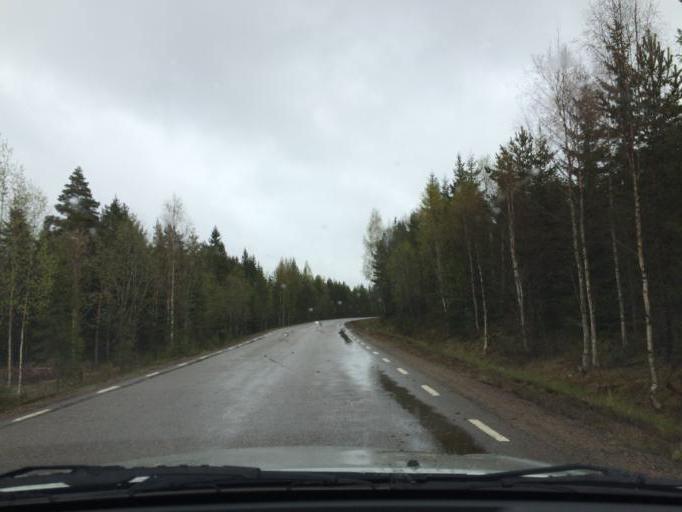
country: SE
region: Dalarna
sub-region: Ludvika Kommun
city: Abborrberget
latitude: 60.0629
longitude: 14.8111
